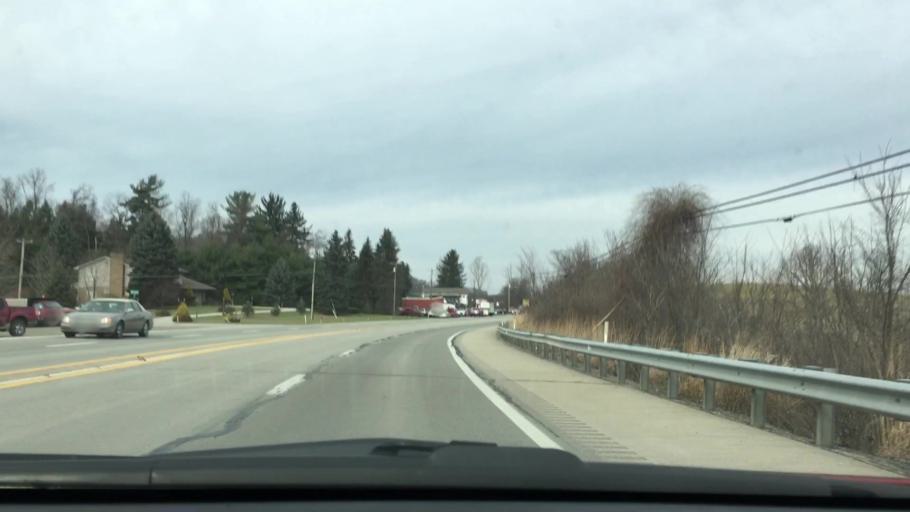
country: US
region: Pennsylvania
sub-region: Fayette County
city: Perryopolis
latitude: 40.1098
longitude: -79.7720
